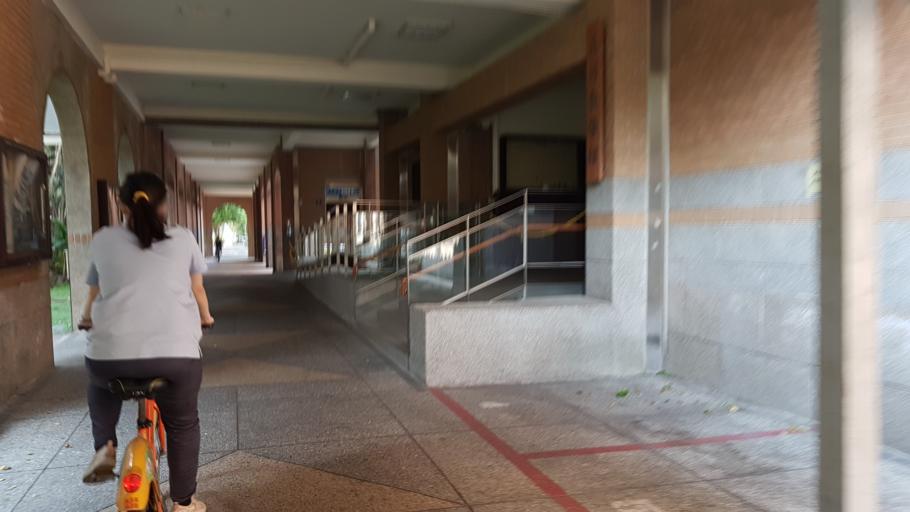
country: TW
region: Taipei
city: Taipei
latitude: 25.0156
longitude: 121.5371
